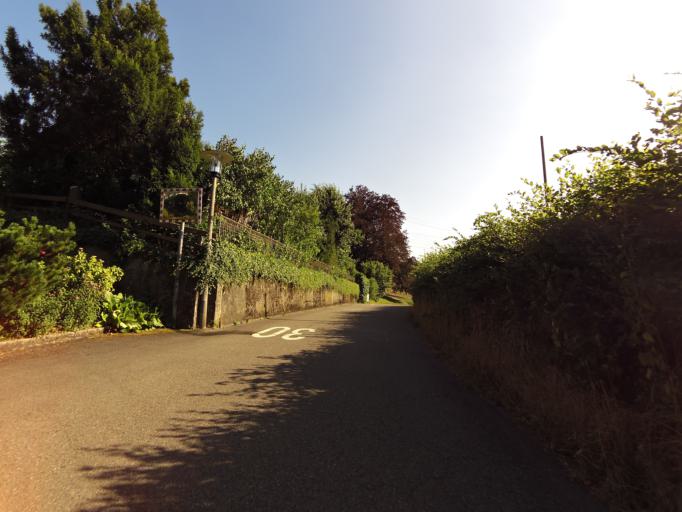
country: CH
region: Aargau
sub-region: Bezirk Lenzburg
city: Lenzburg
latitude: 47.3915
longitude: 8.1813
